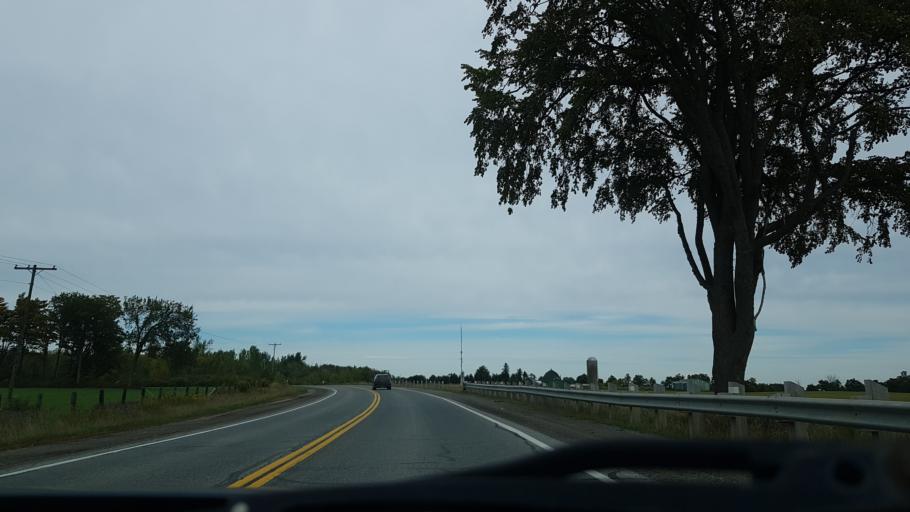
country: CA
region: Ontario
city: Orangeville
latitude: 43.9014
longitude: -79.9494
